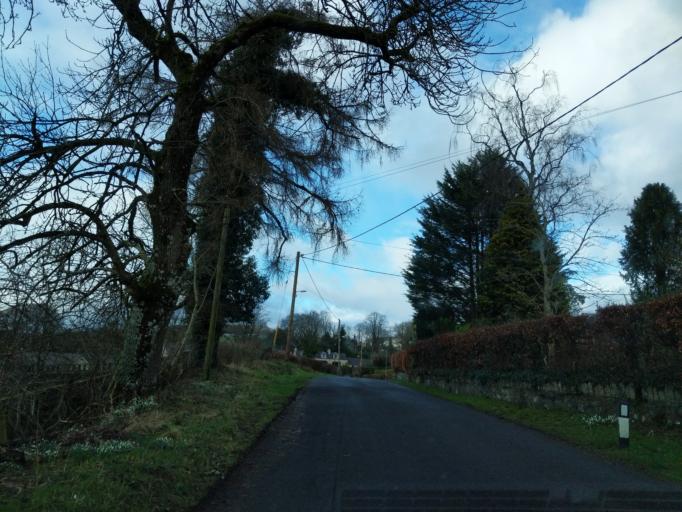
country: GB
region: Scotland
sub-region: Dumfries and Galloway
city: Moffat
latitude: 55.3257
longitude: -3.4307
